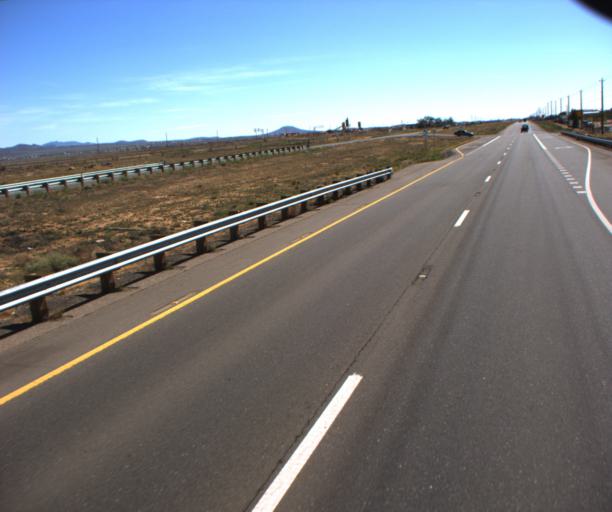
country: US
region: Arizona
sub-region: Mohave County
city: New Kingman-Butler
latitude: 35.2593
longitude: -113.9706
